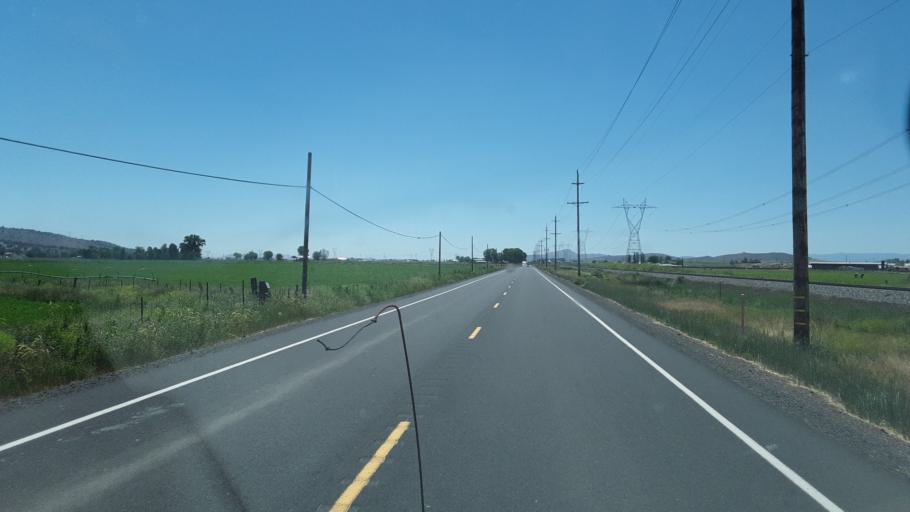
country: US
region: Oregon
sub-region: Klamath County
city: Altamont
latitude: 42.0900
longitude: -121.6859
